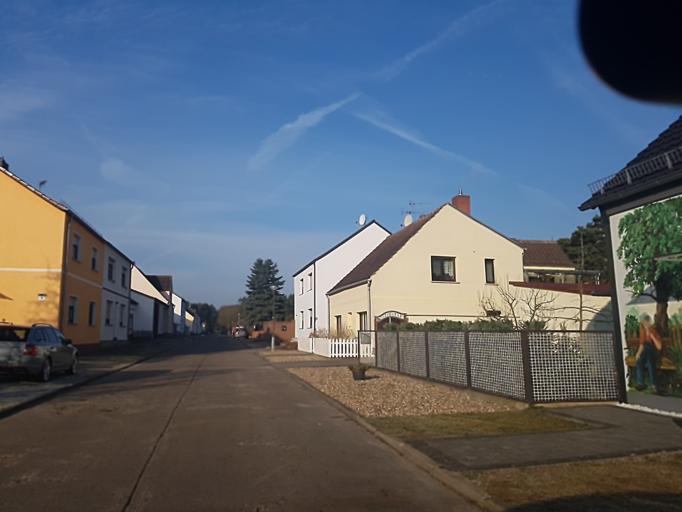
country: DE
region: Brandenburg
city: Wollin
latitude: 52.2806
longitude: 12.4649
